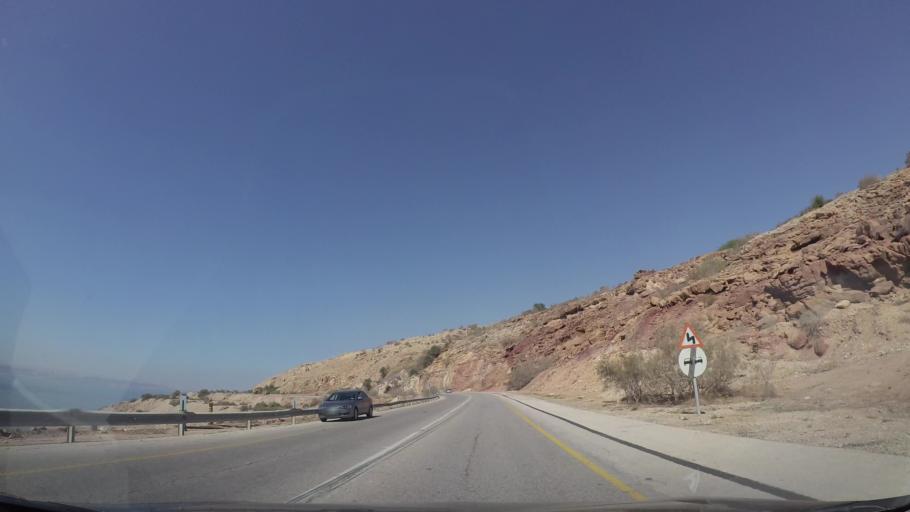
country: JO
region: Madaba
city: Madaba
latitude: 31.5473
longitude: 35.5567
